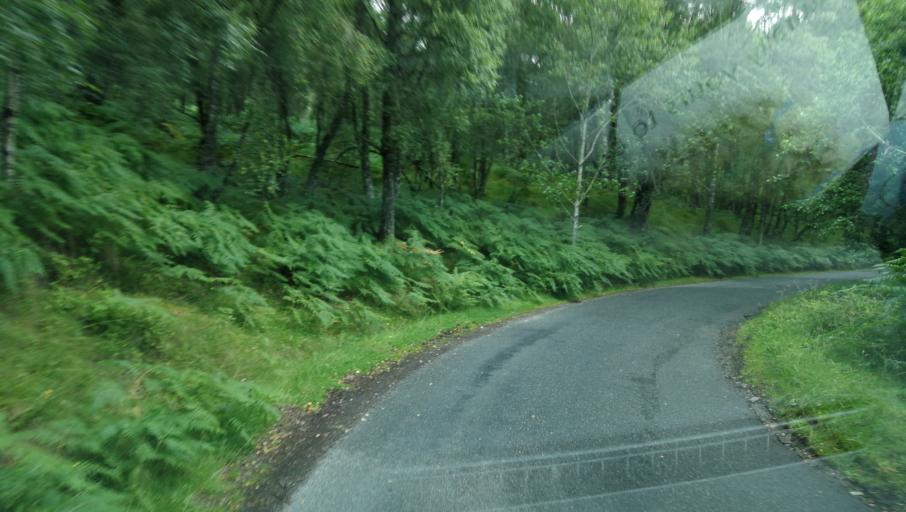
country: GB
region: Scotland
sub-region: Highland
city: Beauly
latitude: 57.3180
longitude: -4.8125
